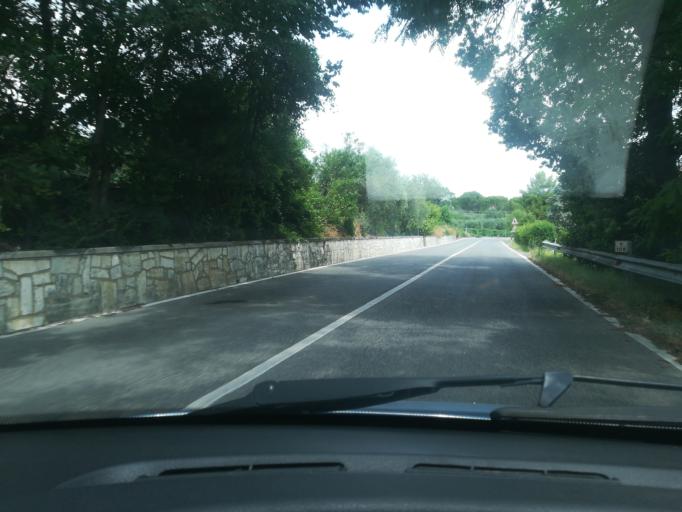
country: IT
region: The Marches
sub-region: Provincia di Macerata
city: Recanati
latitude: 43.3944
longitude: 13.5372
